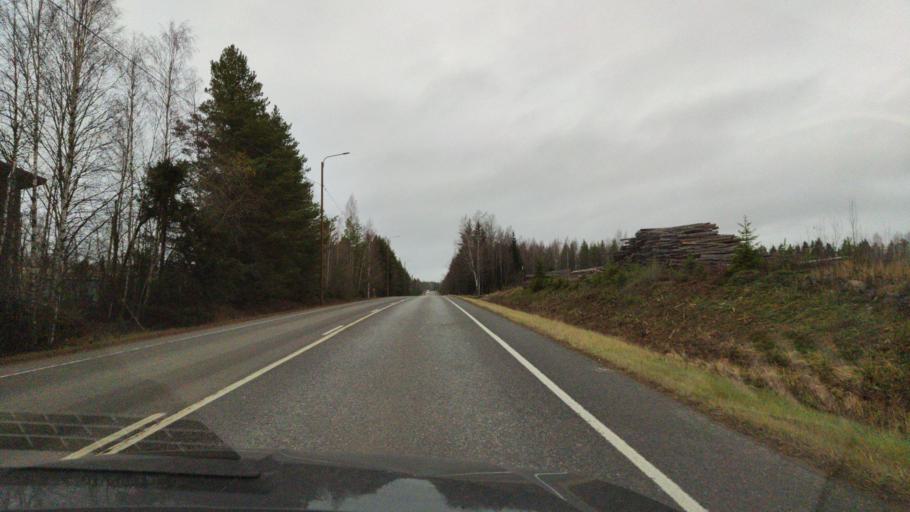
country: FI
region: Satakunta
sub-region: Rauma
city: Kiukainen
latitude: 61.2009
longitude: 22.0534
